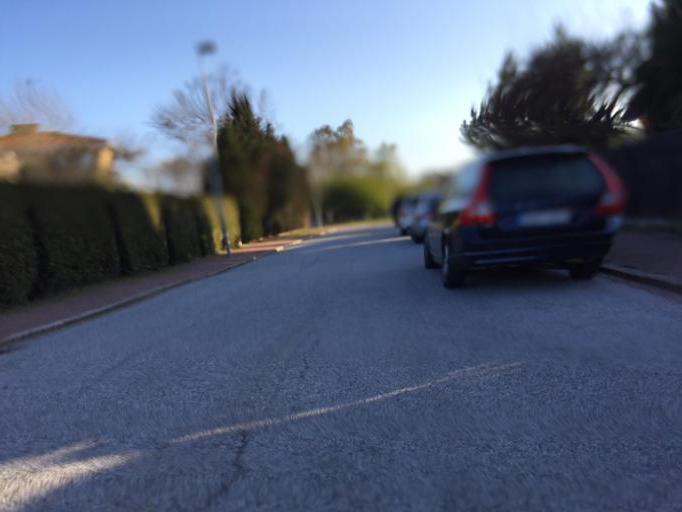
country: SE
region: Skane
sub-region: Malmo
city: Bunkeflostrand
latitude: 55.5833
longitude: 12.9533
